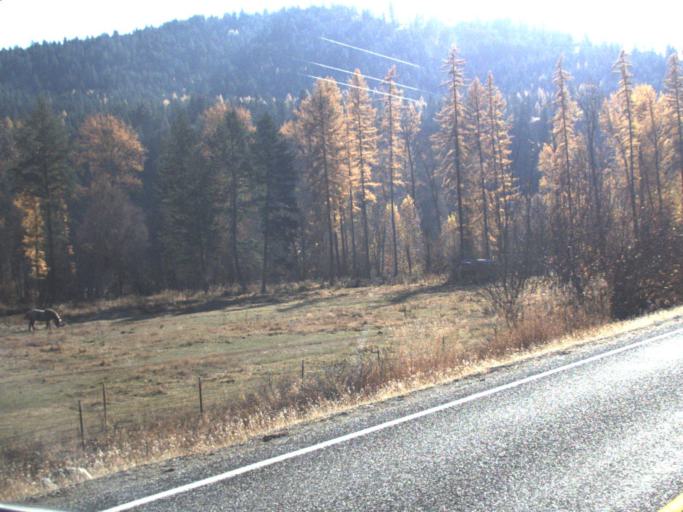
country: CA
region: British Columbia
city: Grand Forks
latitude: 48.9196
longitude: -118.5656
